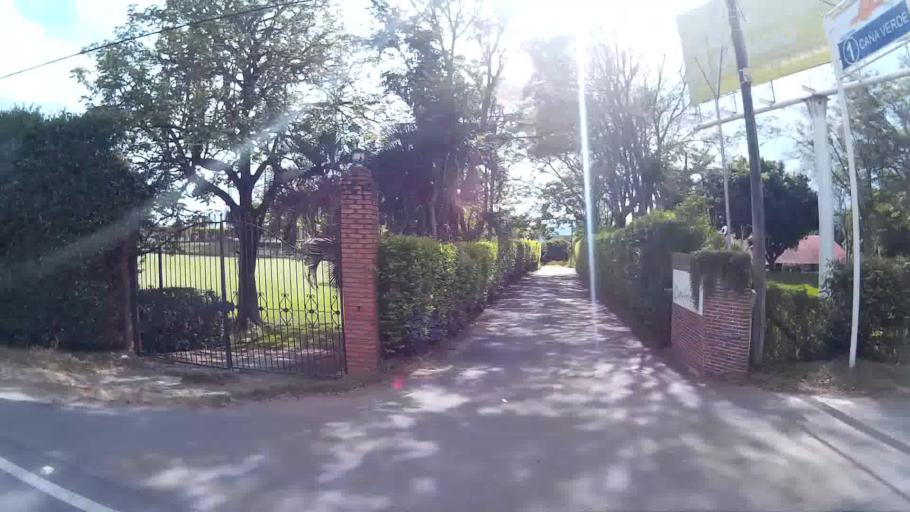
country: CO
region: Valle del Cauca
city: Cartago
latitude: 4.8051
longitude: -75.8428
